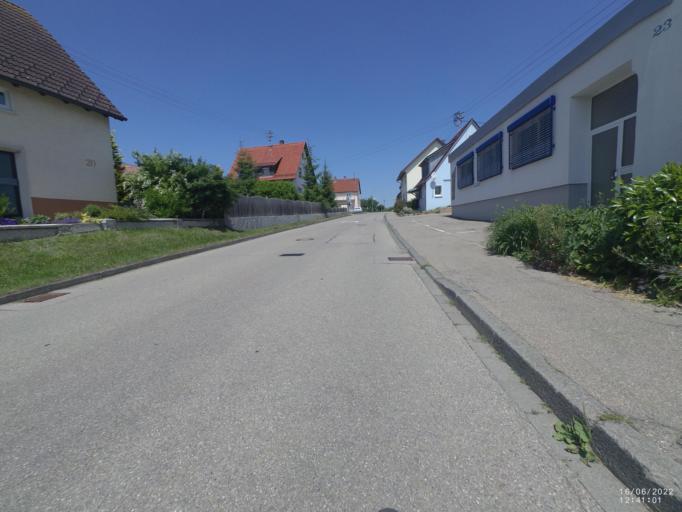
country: DE
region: Baden-Wuerttemberg
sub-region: Tuebingen Region
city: Ballendorf
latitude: 48.5902
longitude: 10.1000
